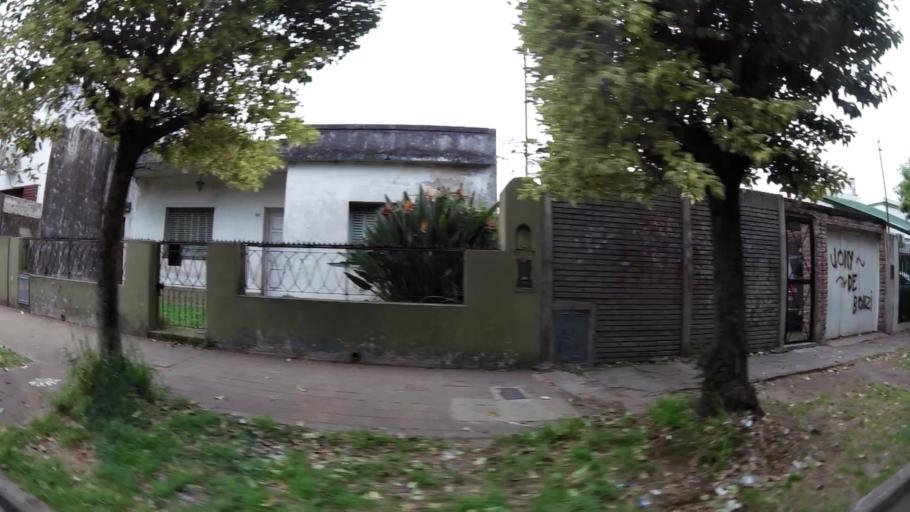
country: AR
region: Buenos Aires F.D.
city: Villa Lugano
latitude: -34.7086
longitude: -58.5175
